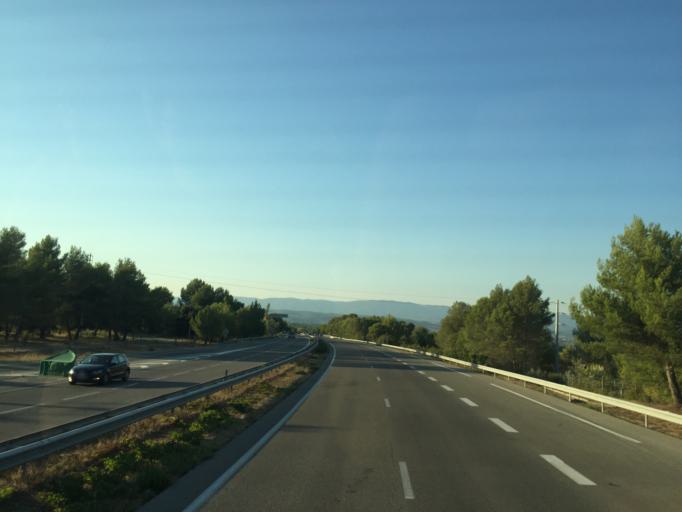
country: FR
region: Provence-Alpes-Cote d'Azur
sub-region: Departement des Bouches-du-Rhone
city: Meyrargues
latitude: 43.6344
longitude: 5.4944
